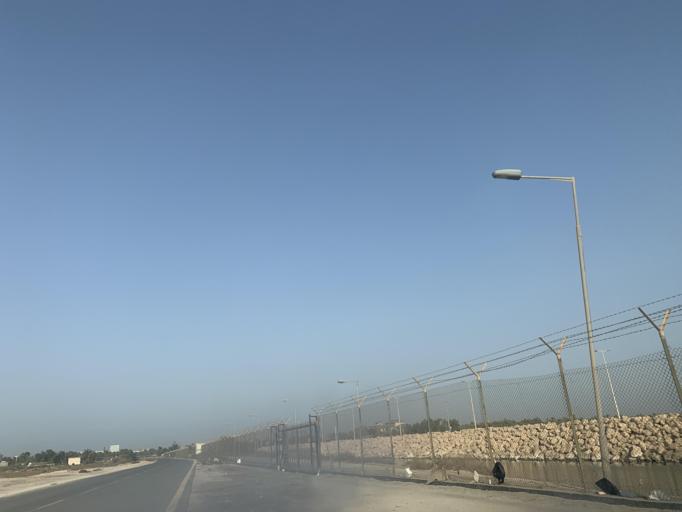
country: BH
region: Central Governorate
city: Madinat Hamad
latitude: 26.1722
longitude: 50.4482
